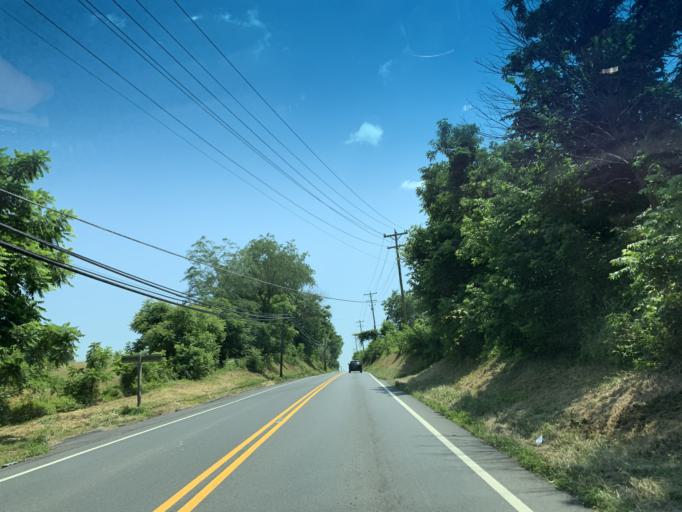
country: US
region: Maryland
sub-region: Frederick County
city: Green Valley
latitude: 39.3686
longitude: -77.2719
